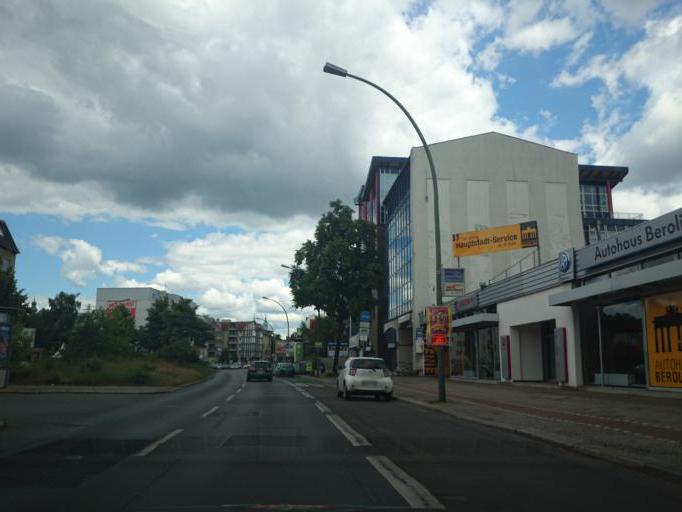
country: DE
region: Berlin
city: Mariendorf
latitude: 52.4364
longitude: 13.3890
